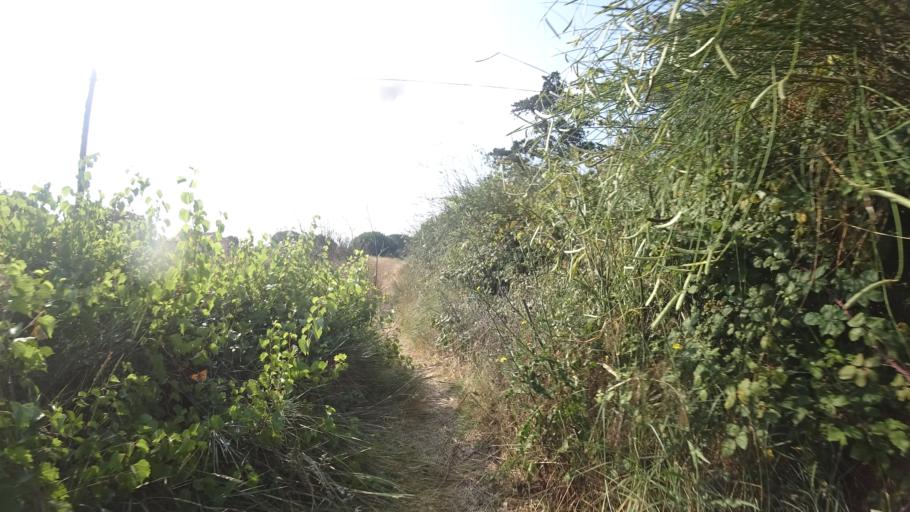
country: FR
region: Languedoc-Roussillon
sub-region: Departement des Pyrenees-Orientales
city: Canet-en-Roussillon
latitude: 42.6896
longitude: 3.0269
